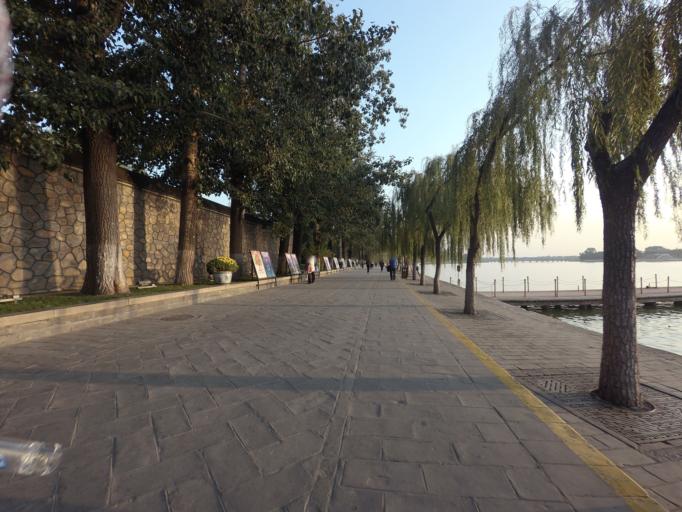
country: CN
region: Beijing
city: Haidian
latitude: 39.9946
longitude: 116.2743
